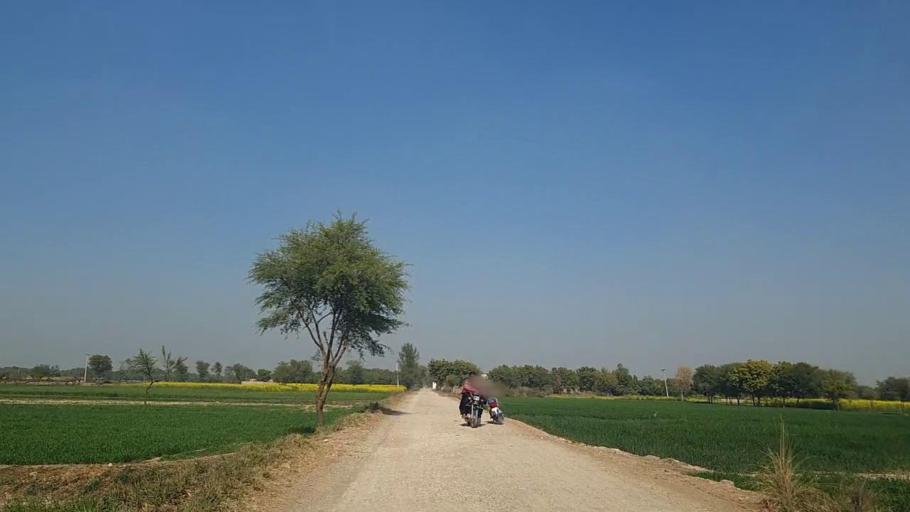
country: PK
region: Sindh
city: Nawabshah
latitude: 26.2371
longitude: 68.3382
